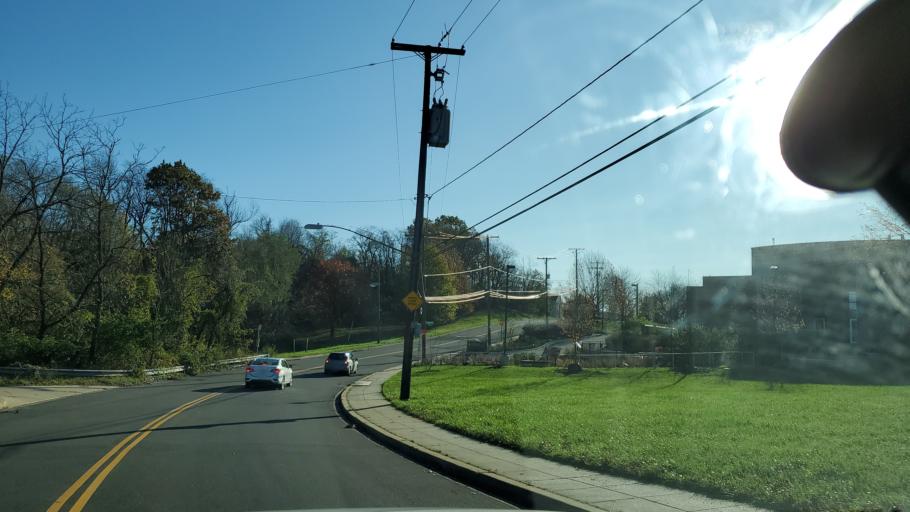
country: US
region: Maryland
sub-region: Prince George's County
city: Hillcrest Heights
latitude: 38.8577
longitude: -76.9772
